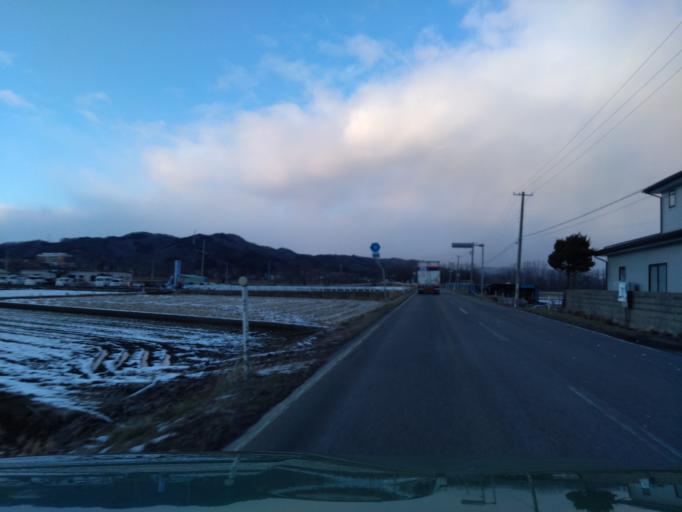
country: JP
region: Iwate
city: Shizukuishi
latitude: 39.6921
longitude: 141.0652
